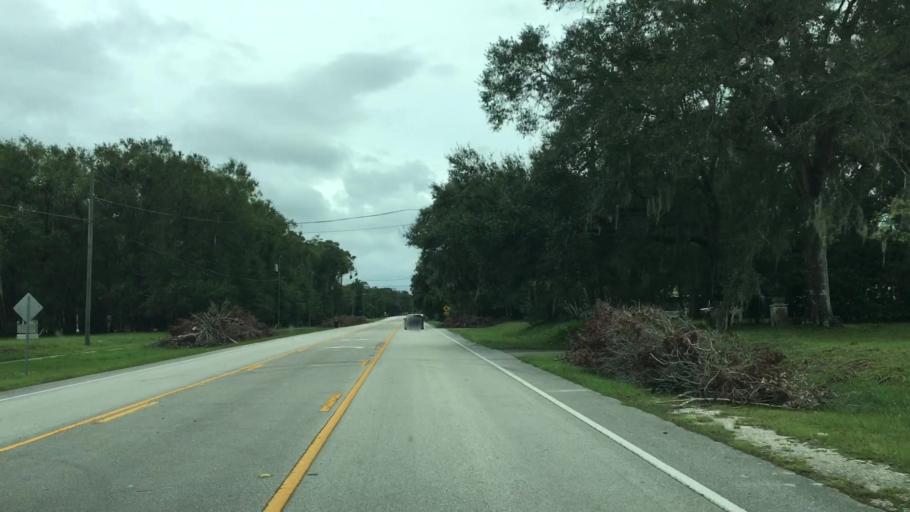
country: US
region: Florida
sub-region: Volusia County
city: Lake Helen
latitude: 28.9862
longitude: -81.2236
